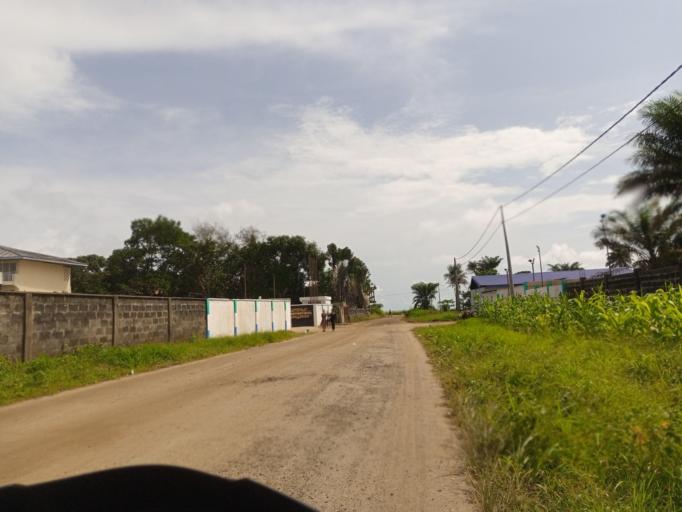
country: SL
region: Northern Province
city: Masoyila
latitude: 8.6132
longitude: -13.2065
